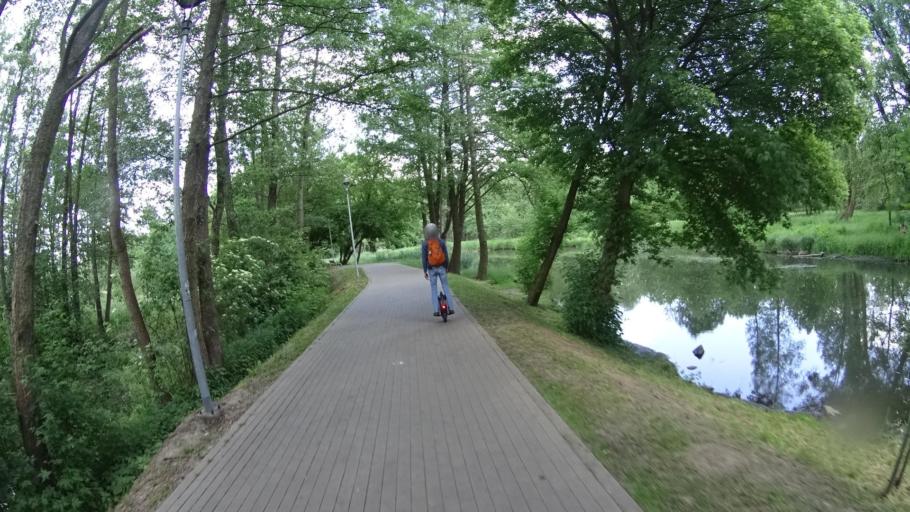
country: PL
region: Masovian Voivodeship
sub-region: Powiat piaseczynski
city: Konstancin-Jeziorna
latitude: 52.0874
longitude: 21.1142
